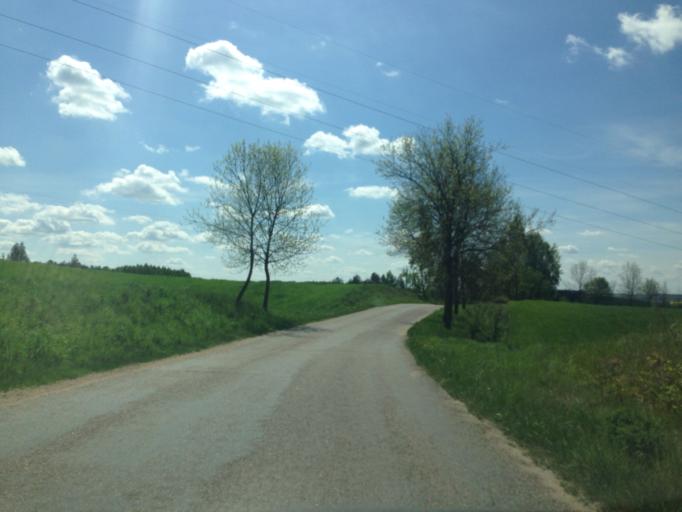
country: PL
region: Kujawsko-Pomorskie
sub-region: Powiat brodnicki
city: Bartniczka
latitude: 53.2832
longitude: 19.6564
